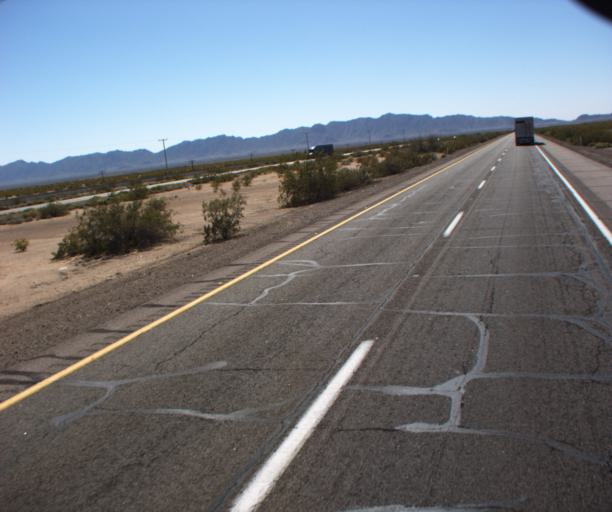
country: US
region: Arizona
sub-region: Yuma County
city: Wellton
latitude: 32.7673
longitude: -113.6188
